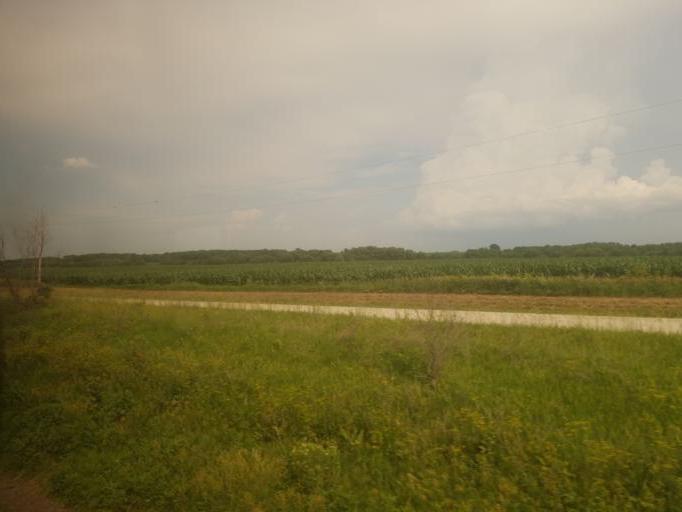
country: US
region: Illinois
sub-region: Henry County
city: Galva
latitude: 41.1010
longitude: -90.1818
